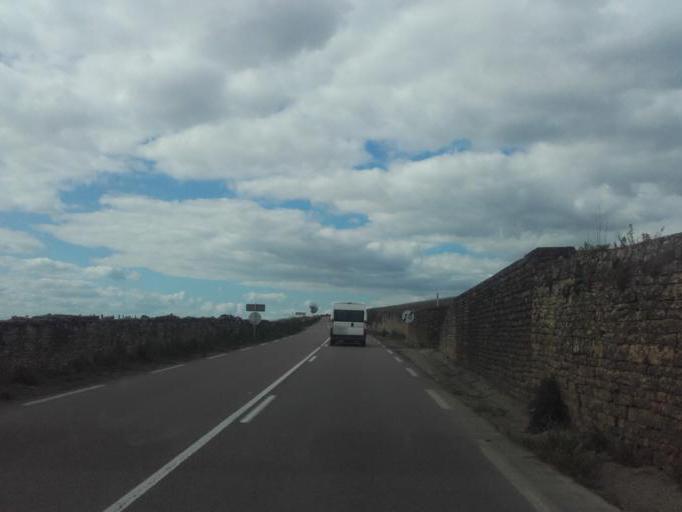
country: FR
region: Bourgogne
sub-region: Departement de la Cote-d'Or
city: Meursault
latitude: 46.9982
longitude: 4.7834
